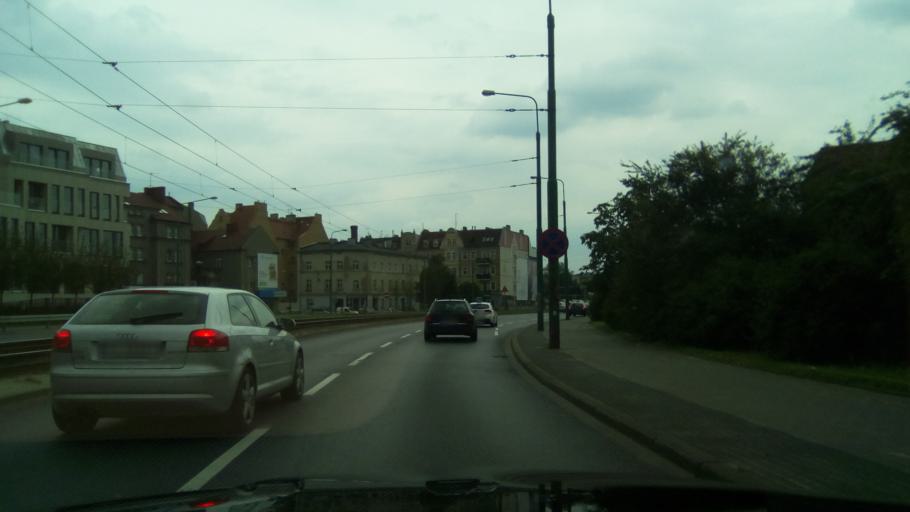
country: PL
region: Greater Poland Voivodeship
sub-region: Poznan
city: Poznan
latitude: 52.4105
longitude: 16.9521
